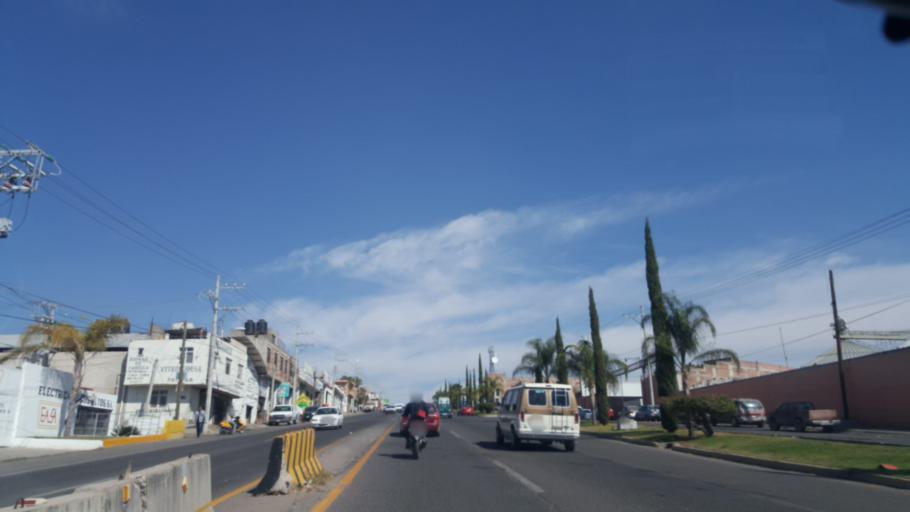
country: MX
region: Jalisco
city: San Juan de los Lagos
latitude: 21.2562
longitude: -102.3251
